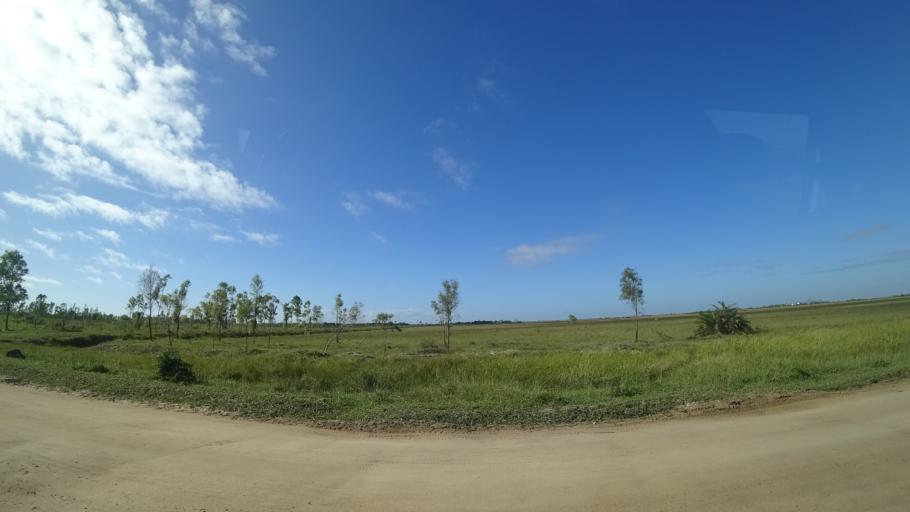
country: MZ
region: Sofala
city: Beira
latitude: -19.7266
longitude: 34.9896
